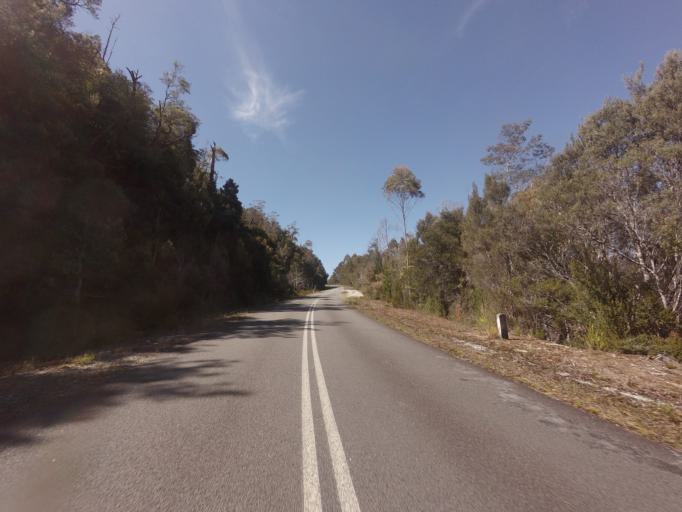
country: AU
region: Tasmania
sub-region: Huon Valley
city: Geeveston
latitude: -42.8581
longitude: 146.2305
